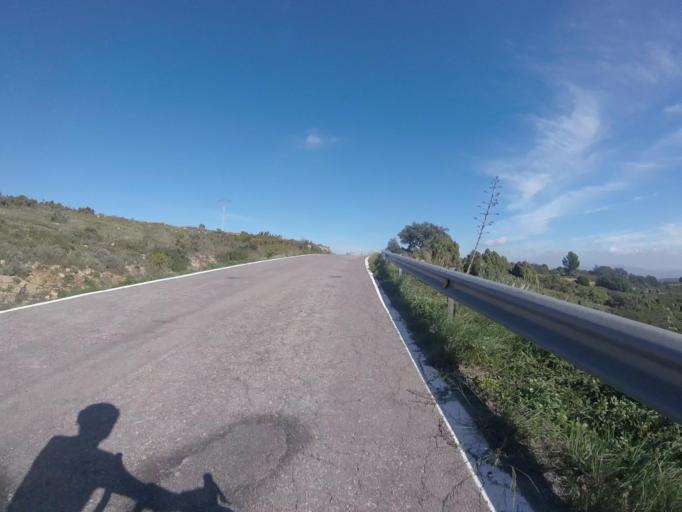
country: ES
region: Valencia
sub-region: Provincia de Castello
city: Sarratella
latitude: 40.3228
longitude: 0.0298
